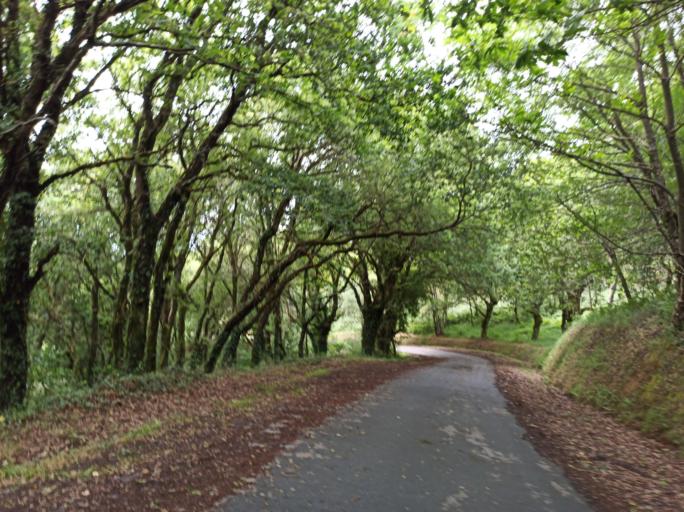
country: ES
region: Galicia
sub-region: Provincia de Pontevedra
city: Silleda
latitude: 42.7703
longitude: -8.1634
